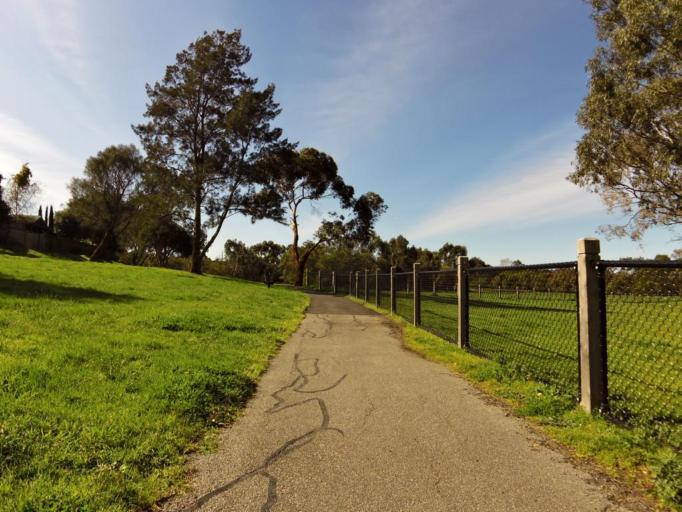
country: AU
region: Victoria
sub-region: Knox
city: Rowville
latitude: -37.9447
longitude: 145.2202
